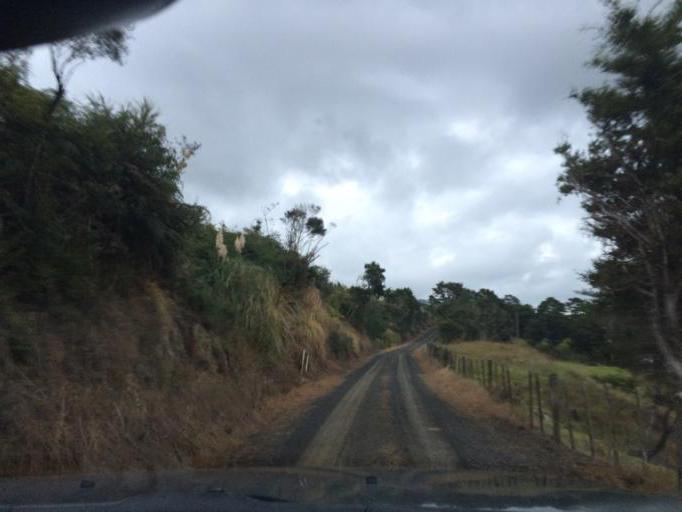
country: NZ
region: Northland
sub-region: Whangarei
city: Maungatapere
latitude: -35.8026
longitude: 174.0650
